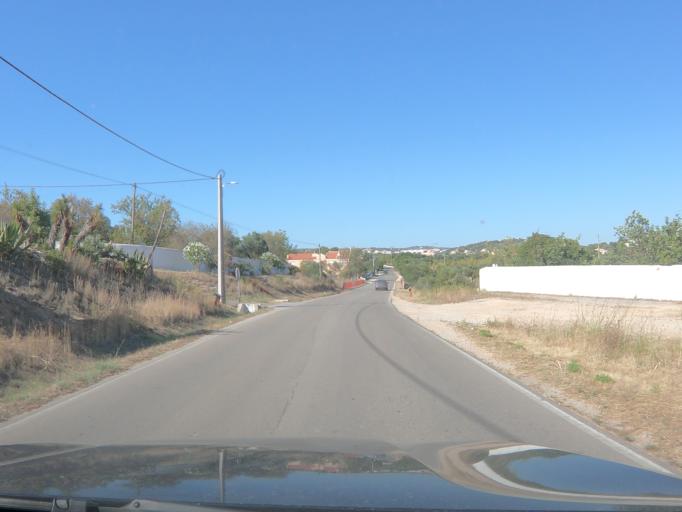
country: PT
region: Faro
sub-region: Loule
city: Loule
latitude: 37.1140
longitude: -8.0261
